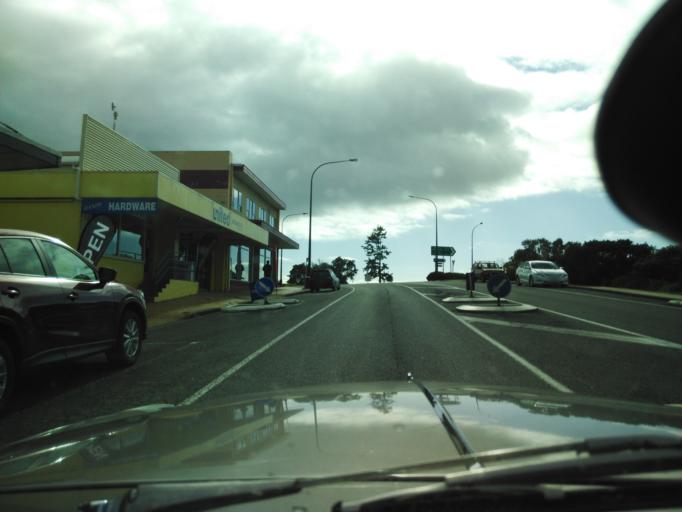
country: NZ
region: Auckland
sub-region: Auckland
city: Wellsford
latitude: -36.2929
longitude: 174.5242
